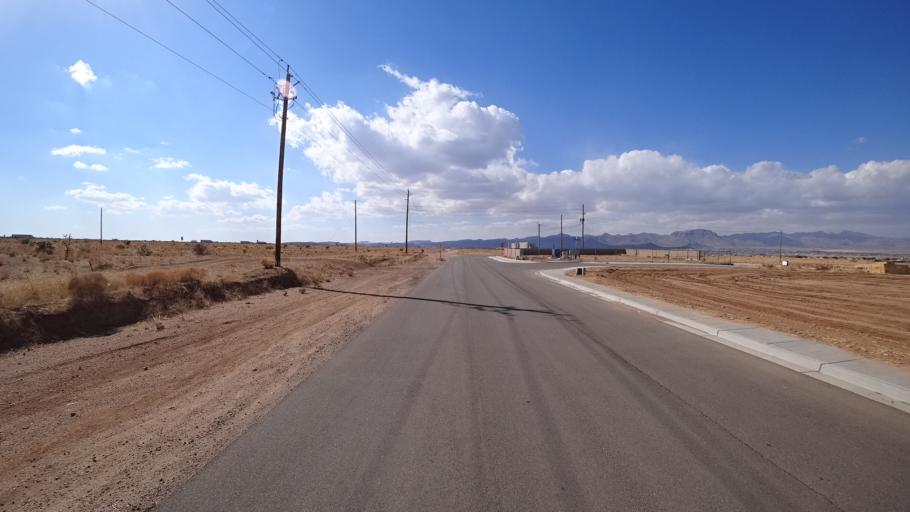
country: US
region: Arizona
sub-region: Mohave County
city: New Kingman-Butler
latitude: 35.2176
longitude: -113.9751
